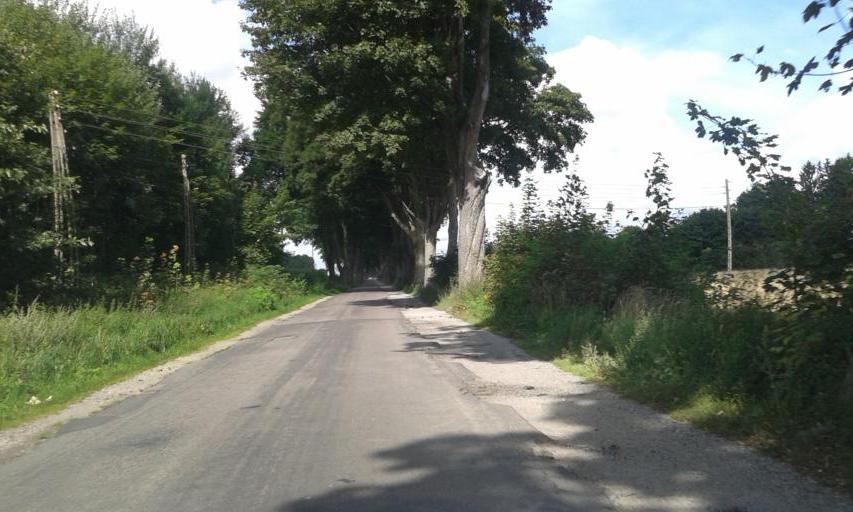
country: PL
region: West Pomeranian Voivodeship
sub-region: Powiat slawienski
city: Slawno
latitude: 54.3097
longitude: 16.6203
